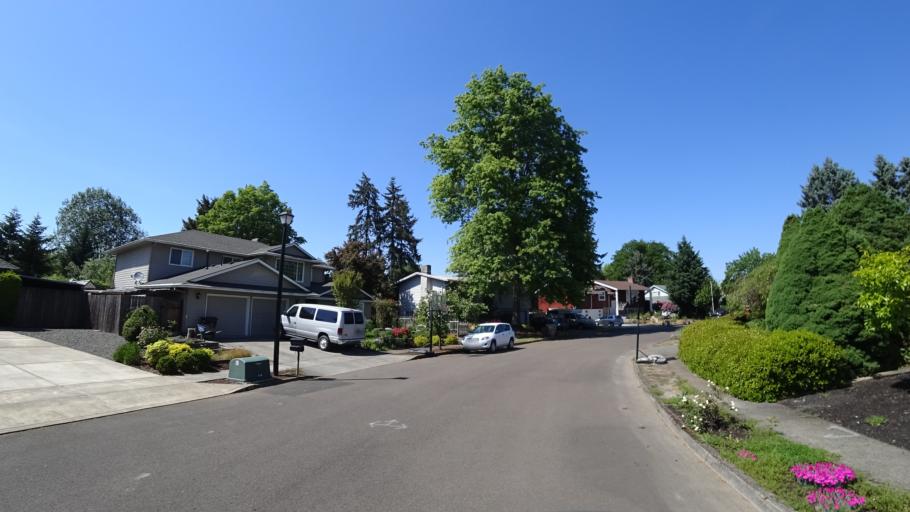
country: US
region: Oregon
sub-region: Washington County
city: Rockcreek
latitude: 45.5497
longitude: -122.8736
